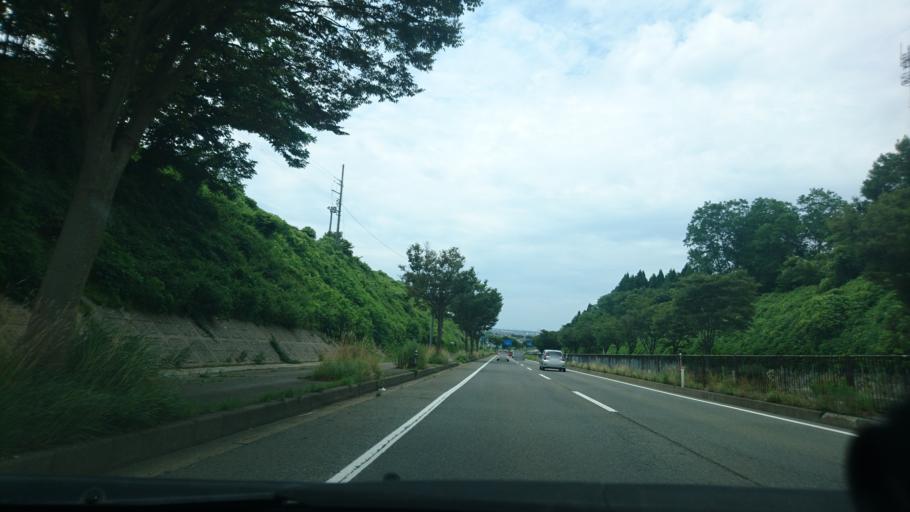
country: JP
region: Akita
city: Akita
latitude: 39.6713
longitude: 140.1586
